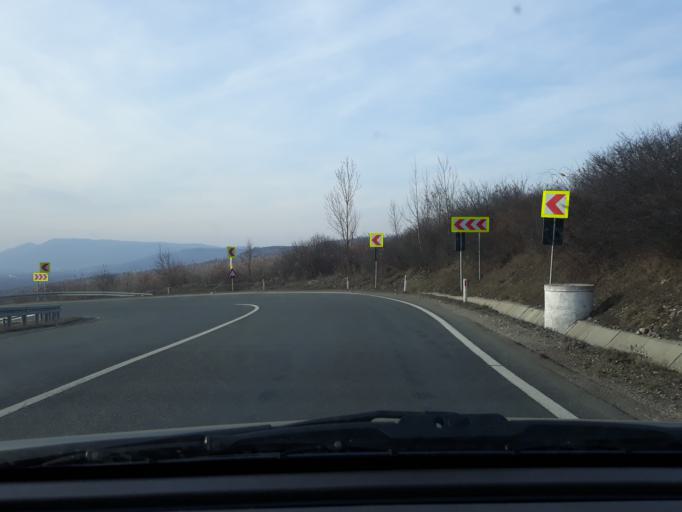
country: RO
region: Salaj
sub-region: Comuna Varsolt
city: Varsolt
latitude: 47.2156
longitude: 22.9286
